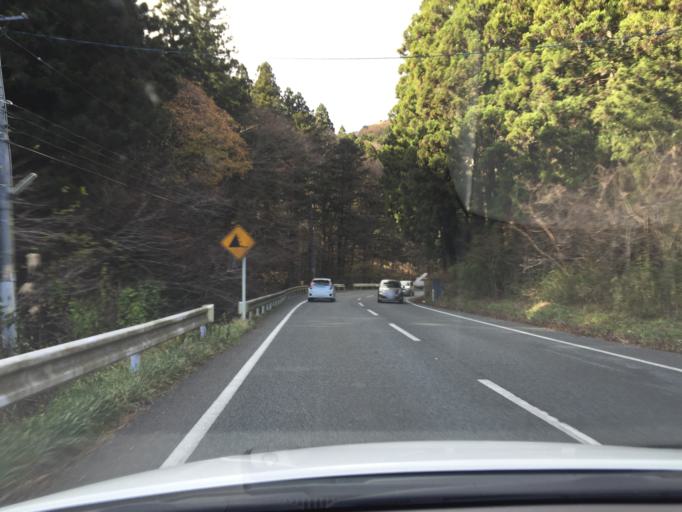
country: JP
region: Fukushima
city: Namie
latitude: 37.6661
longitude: 140.8687
